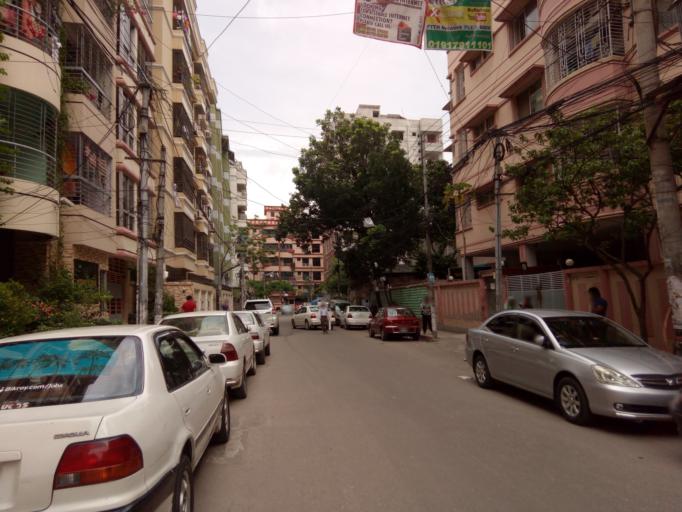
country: BD
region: Dhaka
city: Azimpur
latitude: 23.7456
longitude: 90.3708
